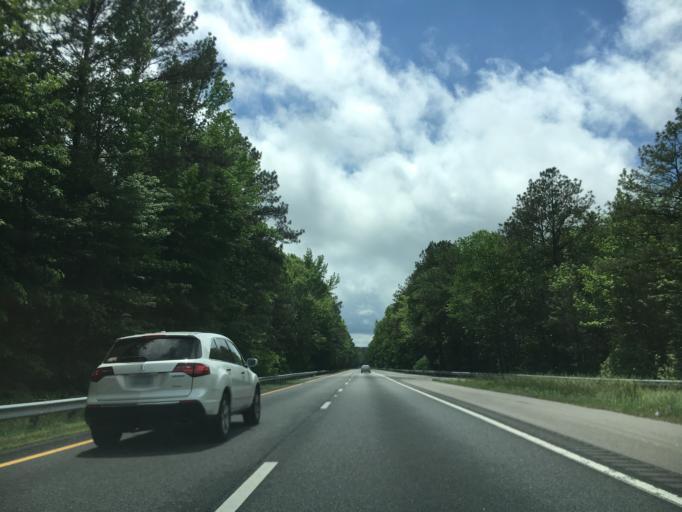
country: US
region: Virginia
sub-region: Brunswick County
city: Lawrenceville
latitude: 36.8442
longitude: -77.9180
